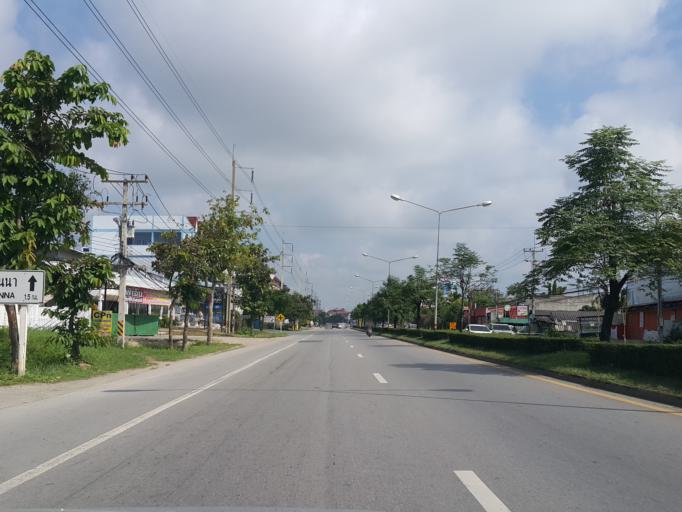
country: TH
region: Chiang Mai
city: San Sai
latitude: 18.8823
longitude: 99.0141
